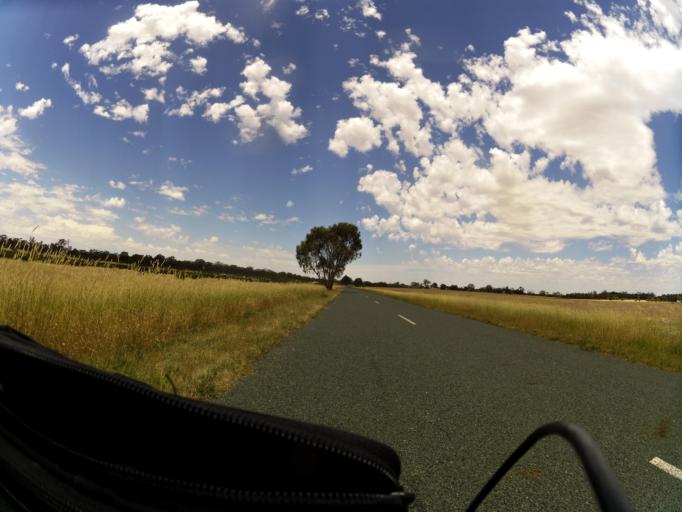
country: AU
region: Victoria
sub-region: Greater Shepparton
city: Shepparton
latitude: -36.6354
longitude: 145.2108
